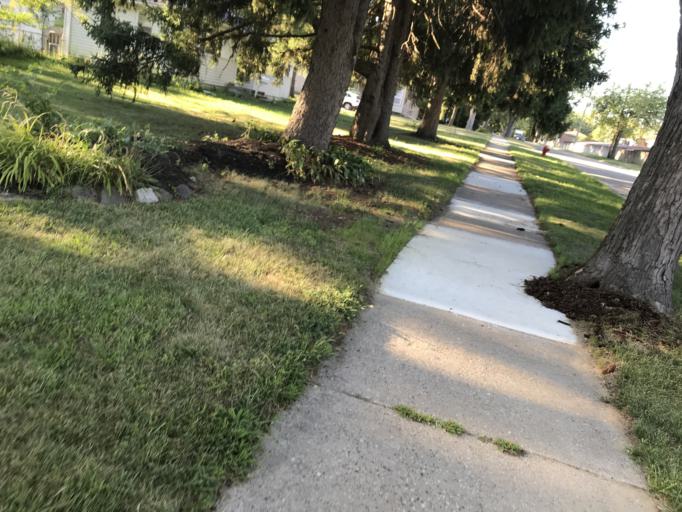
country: US
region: Michigan
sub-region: Oakland County
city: Farmington
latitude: 42.4575
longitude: -83.3518
